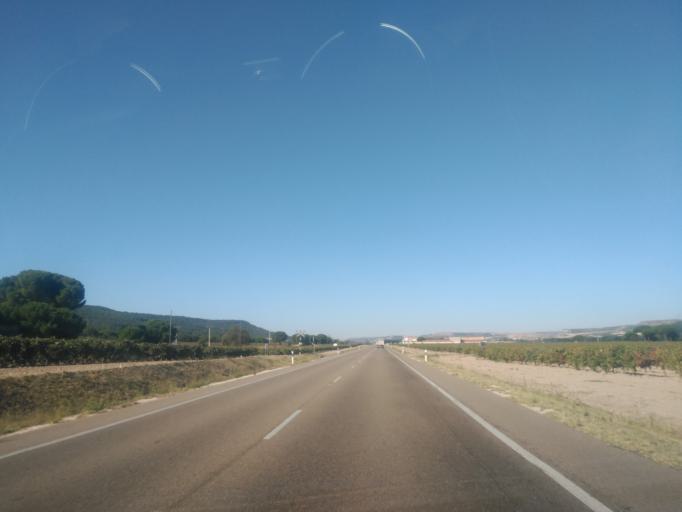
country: ES
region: Castille and Leon
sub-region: Provincia de Valladolid
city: Valbuena de Duero
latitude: 41.6282
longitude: -4.3071
